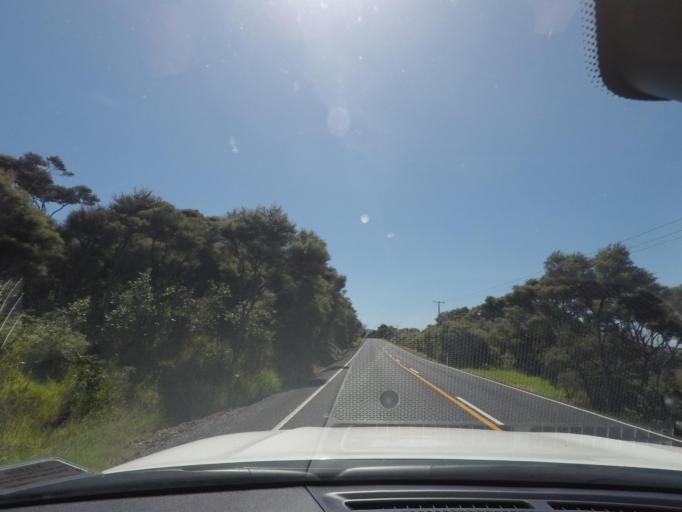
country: NZ
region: Auckland
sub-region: Auckland
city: Parakai
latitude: -36.6312
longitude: 174.3727
